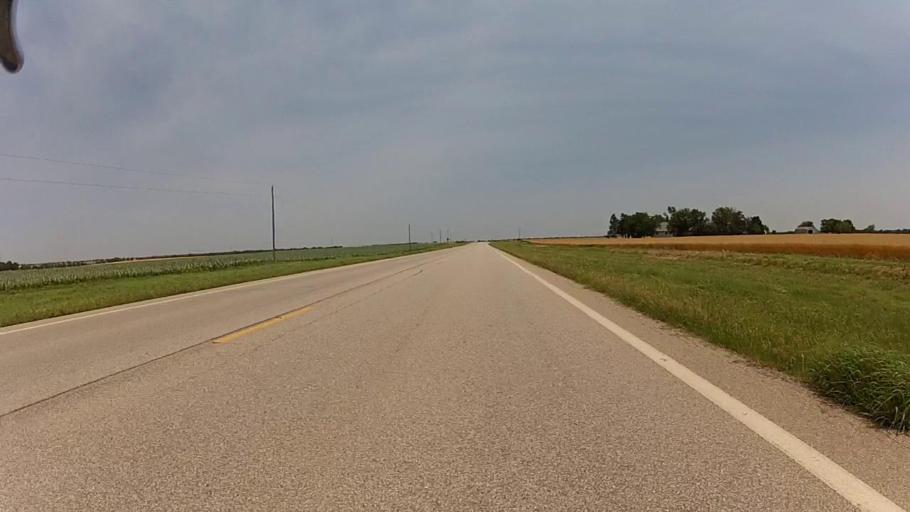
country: US
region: Kansas
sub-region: Cowley County
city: Arkansas City
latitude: 37.0561
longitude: -97.1345
